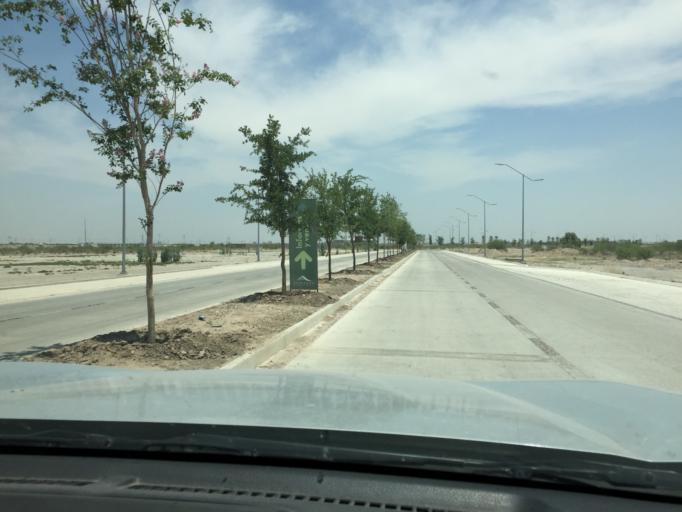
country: MX
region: Durango
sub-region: Gomez Palacio
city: San Jose de Vinedo
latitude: 25.6046
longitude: -103.4399
